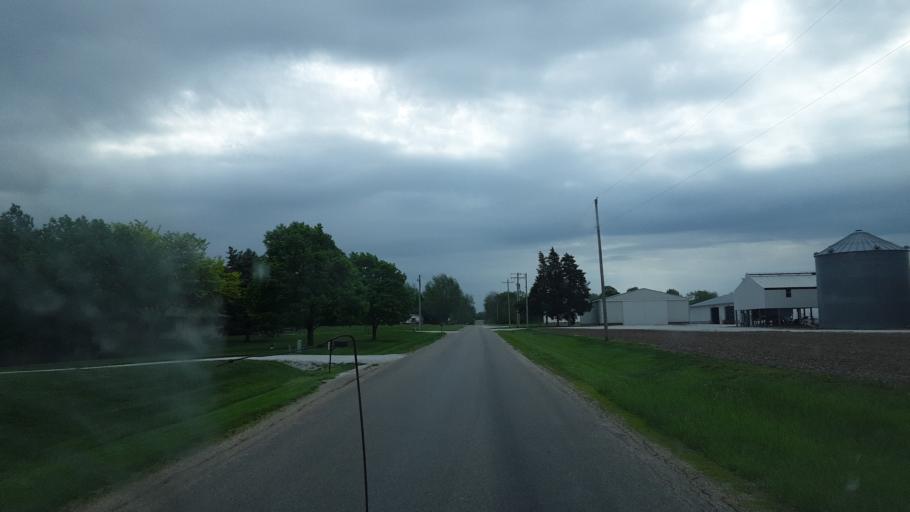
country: US
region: Illinois
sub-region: Fulton County
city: Astoria
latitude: 40.3642
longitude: -90.4333
